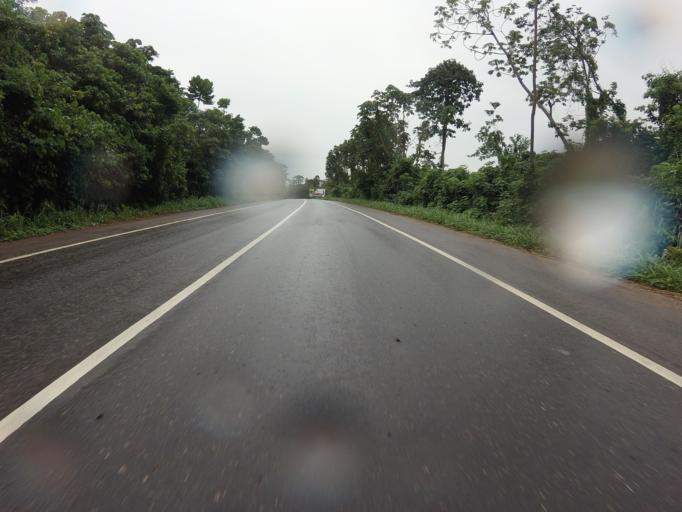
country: GH
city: Kibi
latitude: 6.1478
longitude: -0.4846
